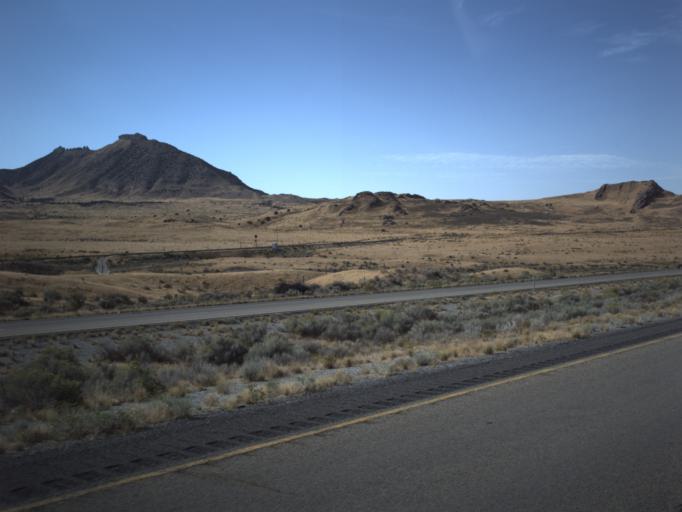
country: US
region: Utah
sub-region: Tooele County
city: Grantsville
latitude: 40.8183
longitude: -112.9121
